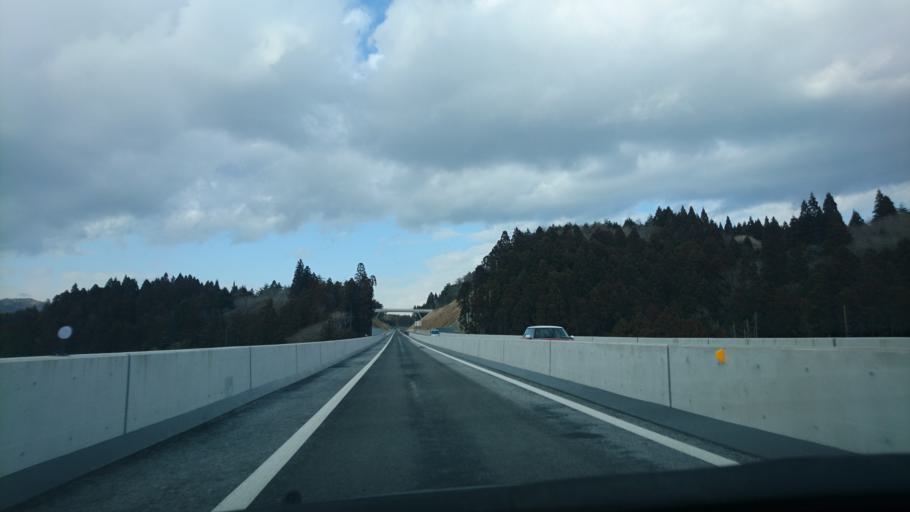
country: JP
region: Miyagi
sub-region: Oshika Gun
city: Onagawa Cho
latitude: 38.7159
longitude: 141.5107
